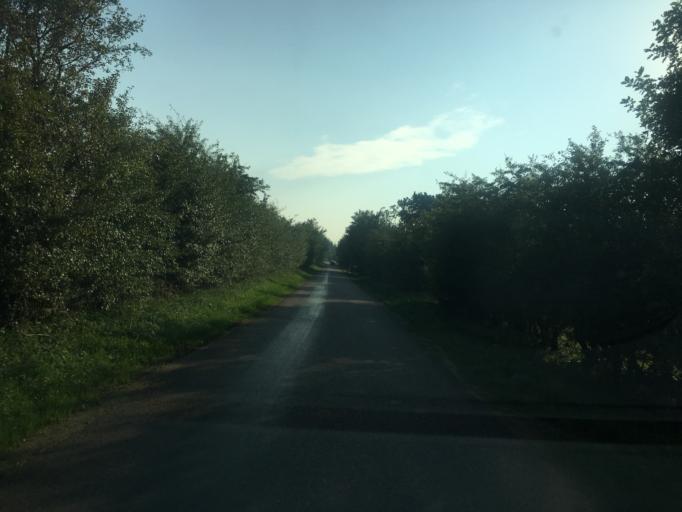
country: DE
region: Schleswig-Holstein
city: Bramstedtlund
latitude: 54.9292
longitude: 9.0606
